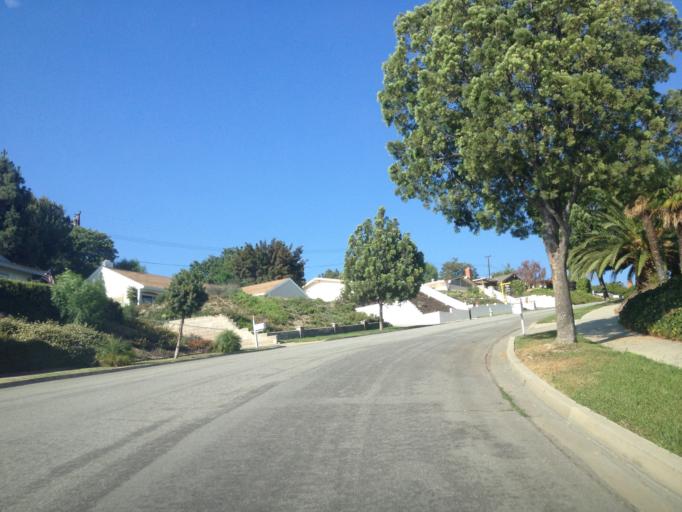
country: US
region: California
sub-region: Orange County
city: Brea
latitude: 33.9379
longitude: -117.9020
